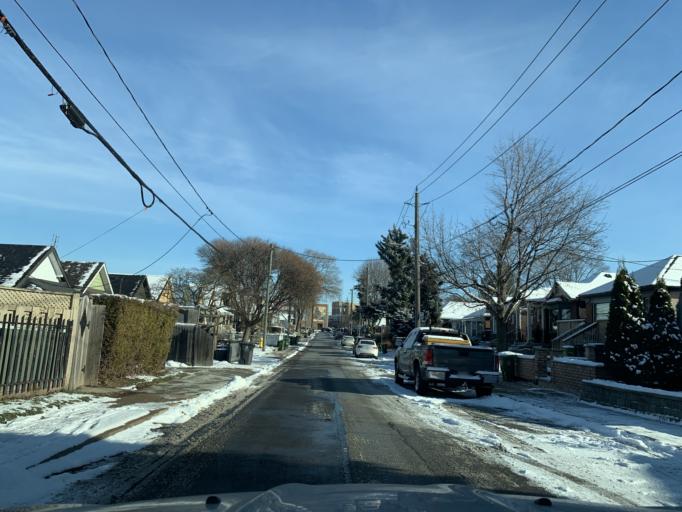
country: CA
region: Ontario
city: Toronto
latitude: 43.6790
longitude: -79.4776
